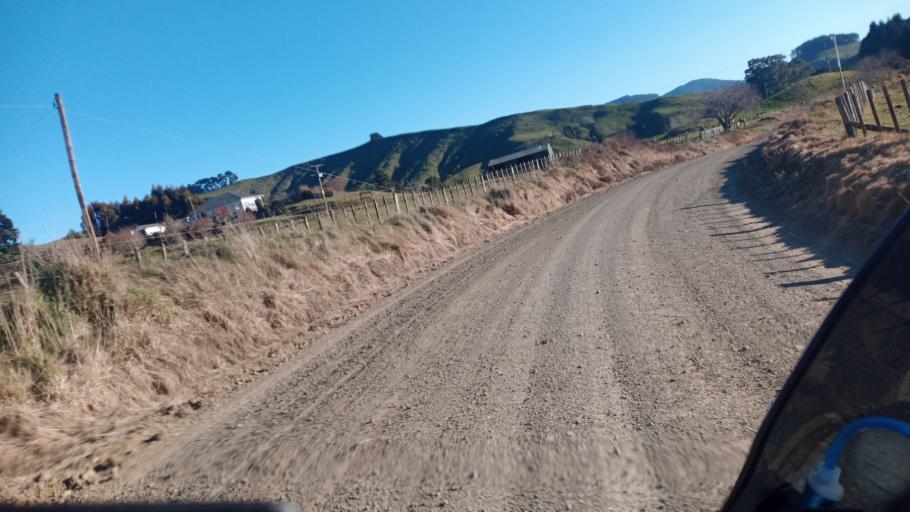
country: NZ
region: Bay of Plenty
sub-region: Opotiki District
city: Opotiki
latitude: -38.4587
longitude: 177.4293
